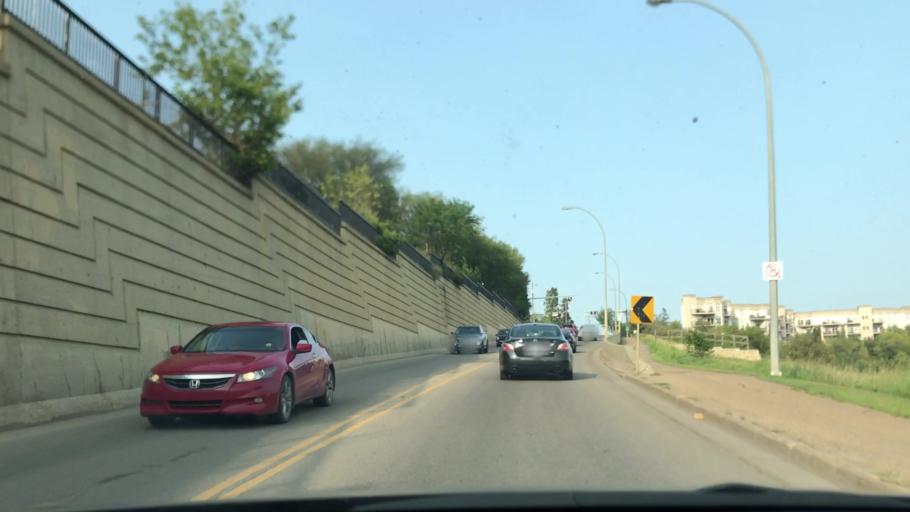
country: CA
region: Alberta
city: Edmonton
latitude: 53.5425
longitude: -113.4828
